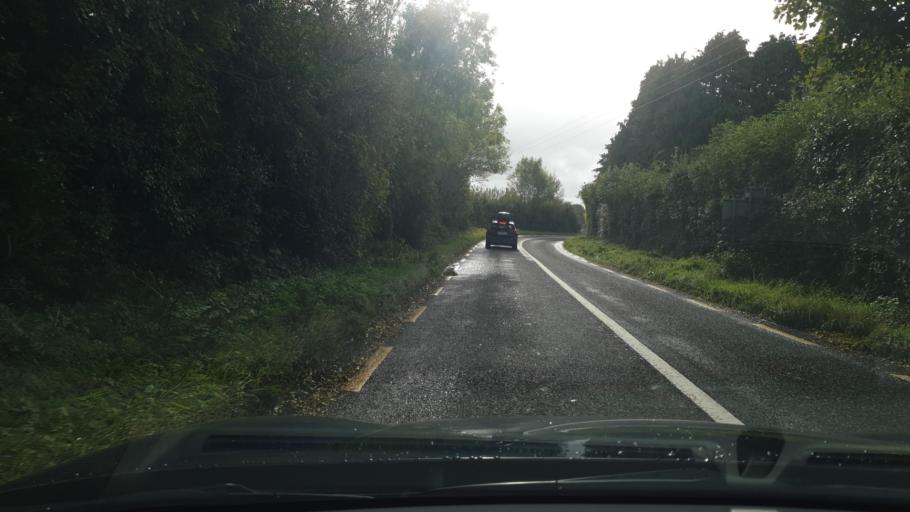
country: IE
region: Leinster
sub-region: An Mhi
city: Dunshaughlin
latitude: 53.5197
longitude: -6.5301
